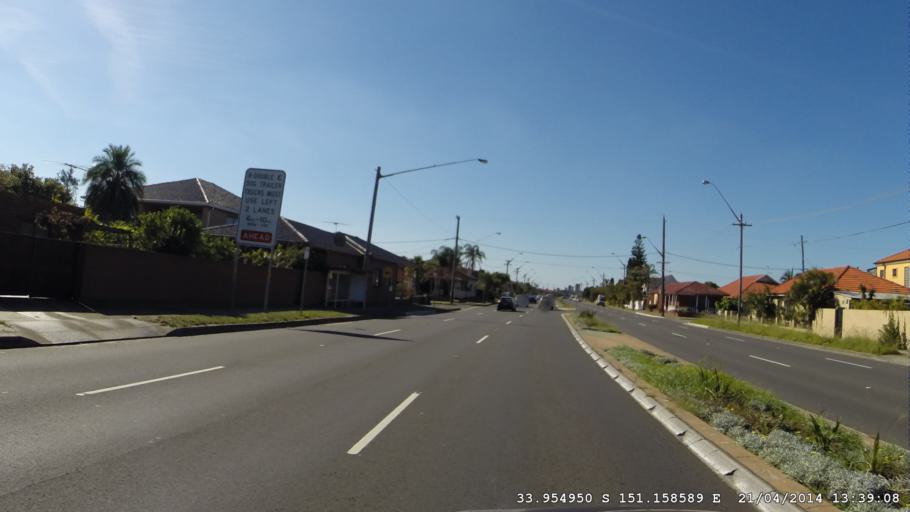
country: AU
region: New South Wales
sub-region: Rockdale
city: Brighton-Le-Sands
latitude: -33.9549
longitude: 151.1586
